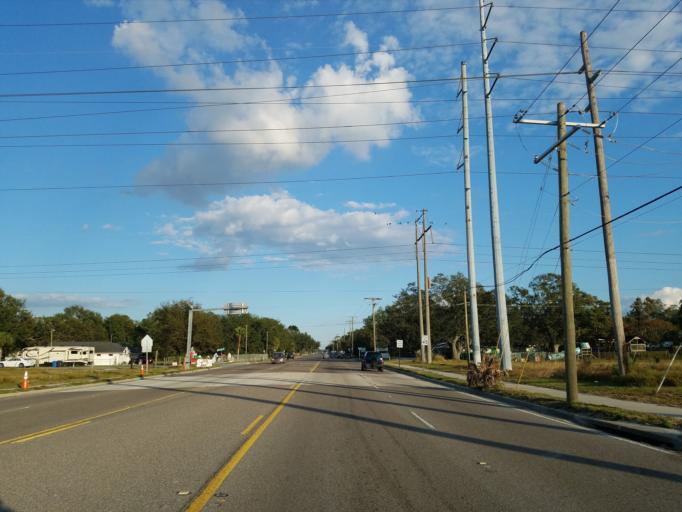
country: US
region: Florida
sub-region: Hillsborough County
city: Gibsonton
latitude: 27.8498
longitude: -82.3679
